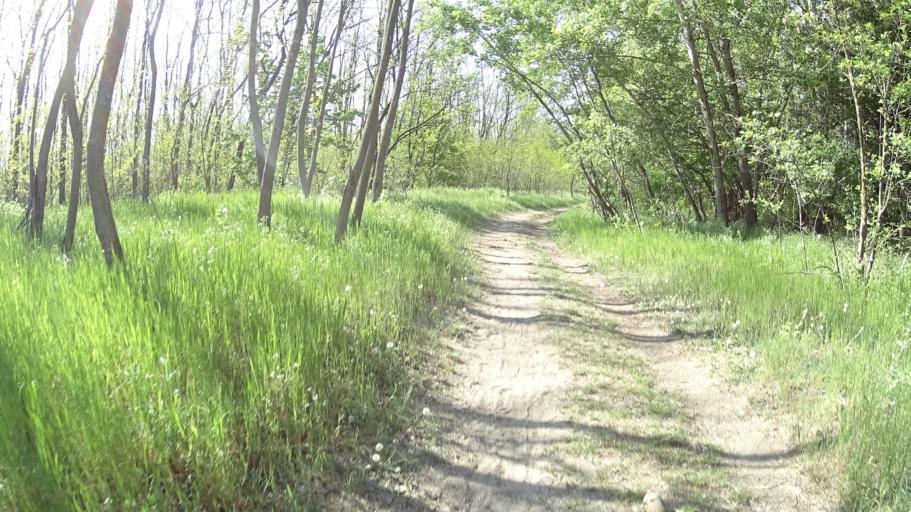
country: HU
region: Pest
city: Vecses
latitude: 47.4469
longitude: 19.2796
